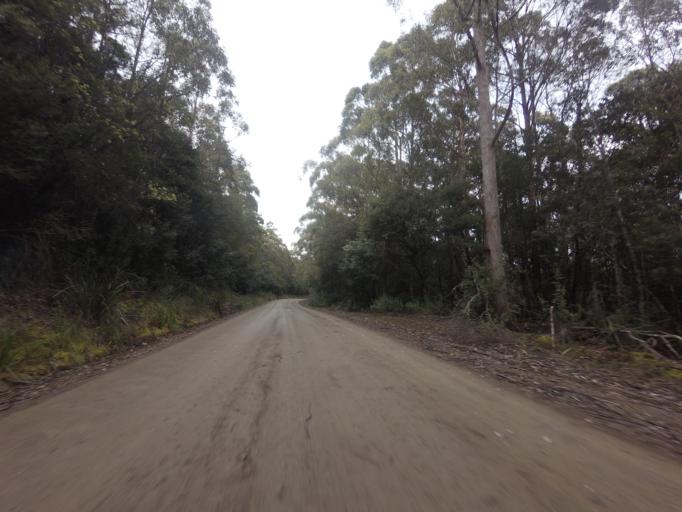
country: AU
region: Tasmania
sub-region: Huon Valley
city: Geeveston
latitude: -43.5005
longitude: 146.8780
